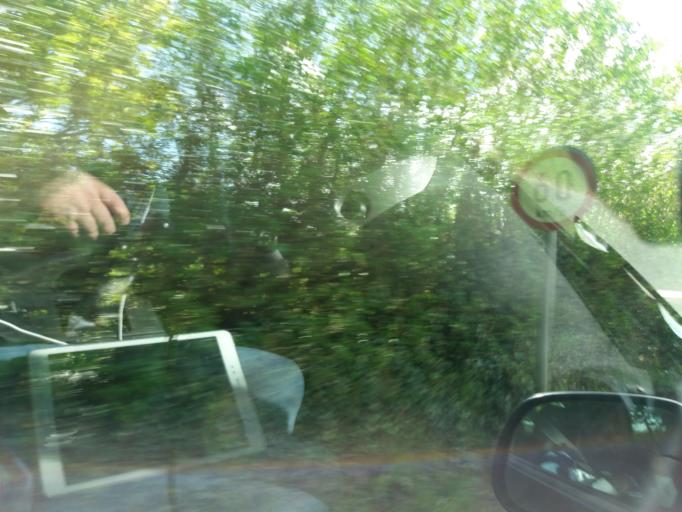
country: IE
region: Munster
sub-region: Waterford
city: Dunmore East
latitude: 52.2419
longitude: -6.9445
